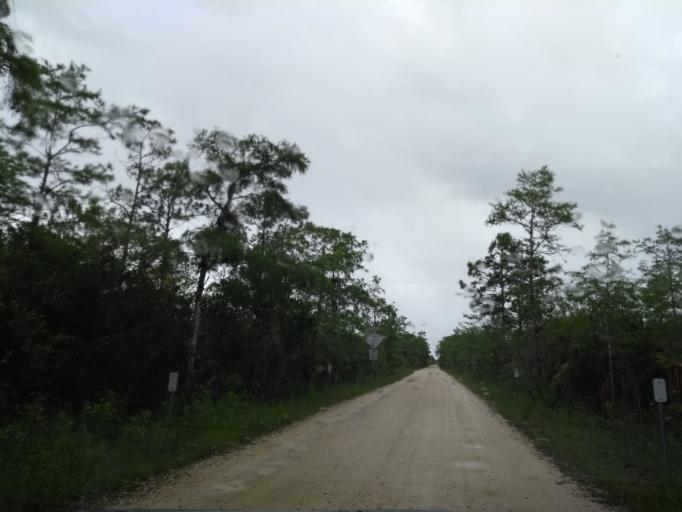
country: US
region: Florida
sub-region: Miami-Dade County
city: The Hammocks
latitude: 25.7604
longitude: -81.0092
